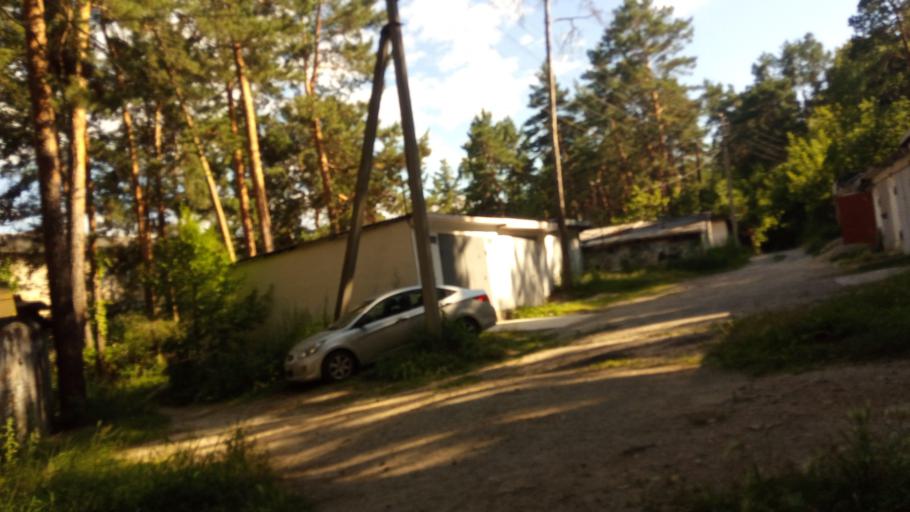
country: RU
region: Chelyabinsk
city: Chebarkul'
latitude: 55.0186
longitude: 60.3161
